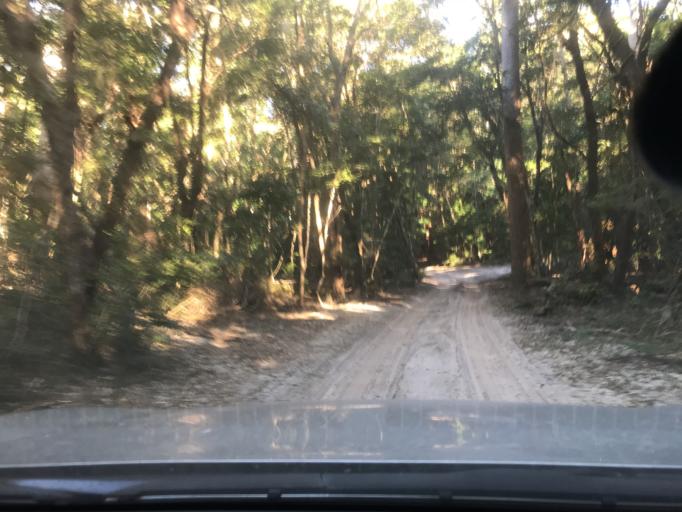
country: AU
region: Queensland
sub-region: Fraser Coast
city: Urangan
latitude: -25.3259
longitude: 153.1505
